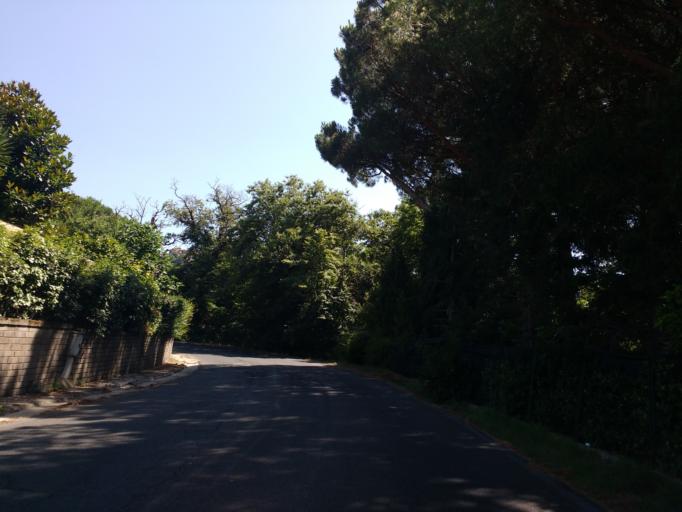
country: IT
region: Latium
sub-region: Citta metropolitana di Roma Capitale
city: Rocca di Papa
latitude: 41.7677
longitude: 12.7096
